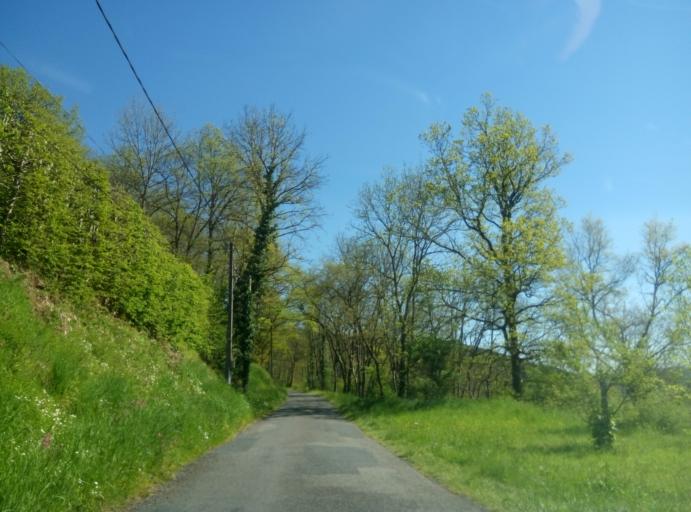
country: FR
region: Rhone-Alpes
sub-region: Departement du Rhone
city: Grandris
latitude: 46.0560
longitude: 4.4959
